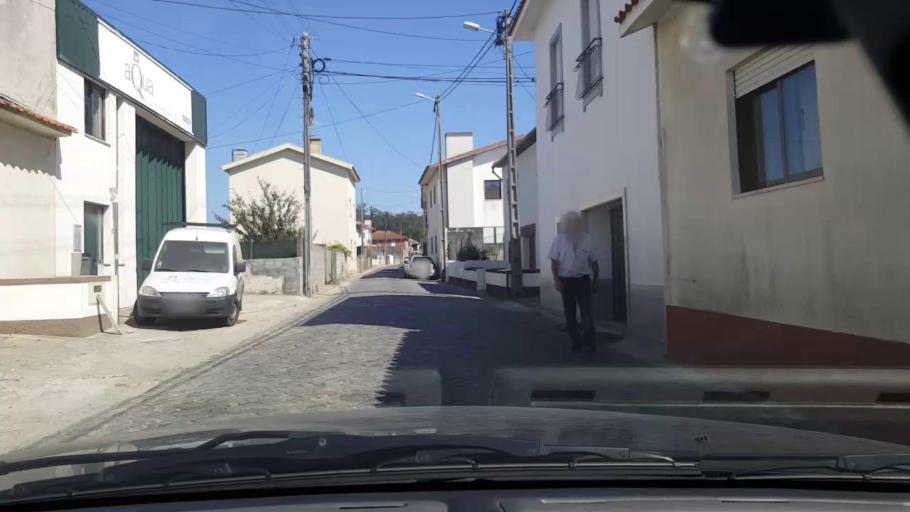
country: PT
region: Porto
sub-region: Matosinhos
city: Lavra
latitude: 41.2970
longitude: -8.7191
